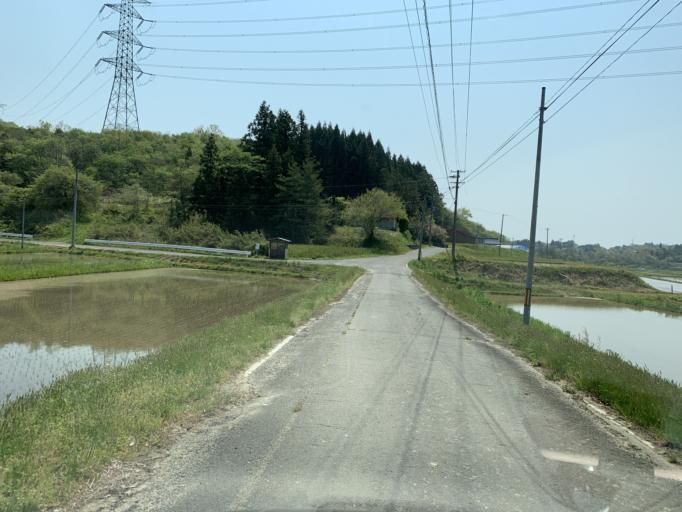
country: JP
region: Iwate
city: Ichinoseki
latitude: 38.8562
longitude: 141.0855
